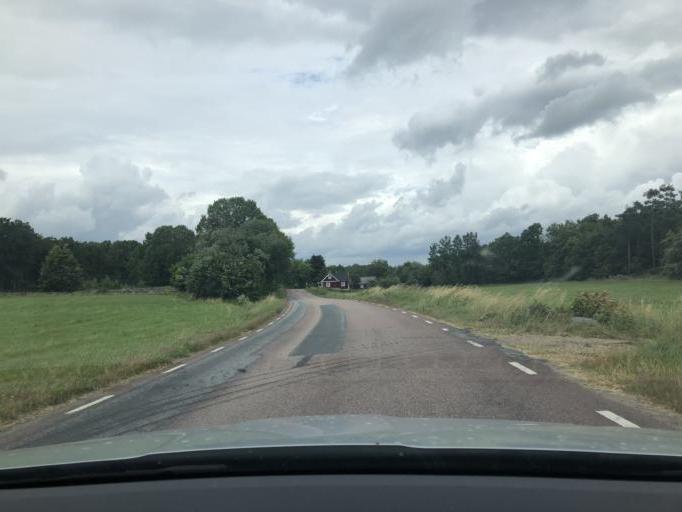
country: SE
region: Blekinge
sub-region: Solvesborgs Kommun
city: Soelvesborg
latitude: 56.1360
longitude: 14.6077
